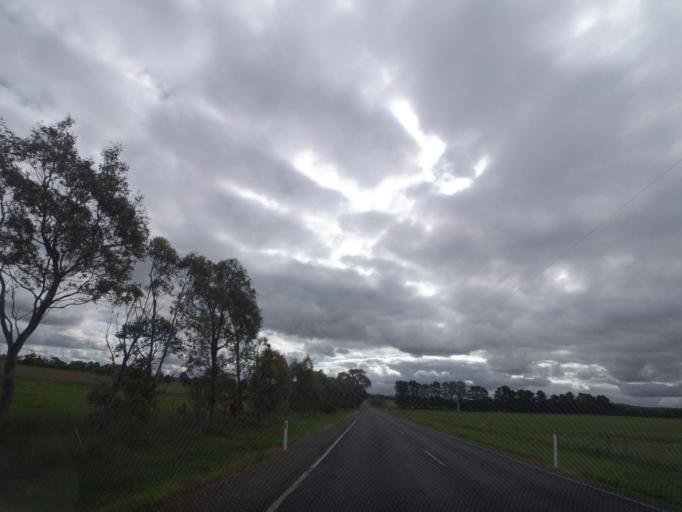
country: AU
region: Victoria
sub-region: Whittlesea
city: Whittlesea
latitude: -37.5256
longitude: 145.0845
